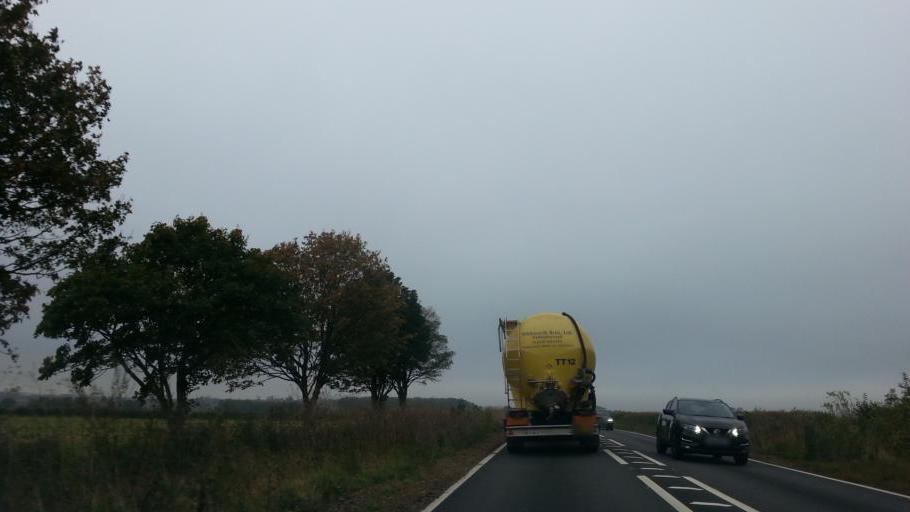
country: GB
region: England
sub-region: Northamptonshire
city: Oundle
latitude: 52.4314
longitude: -0.4836
